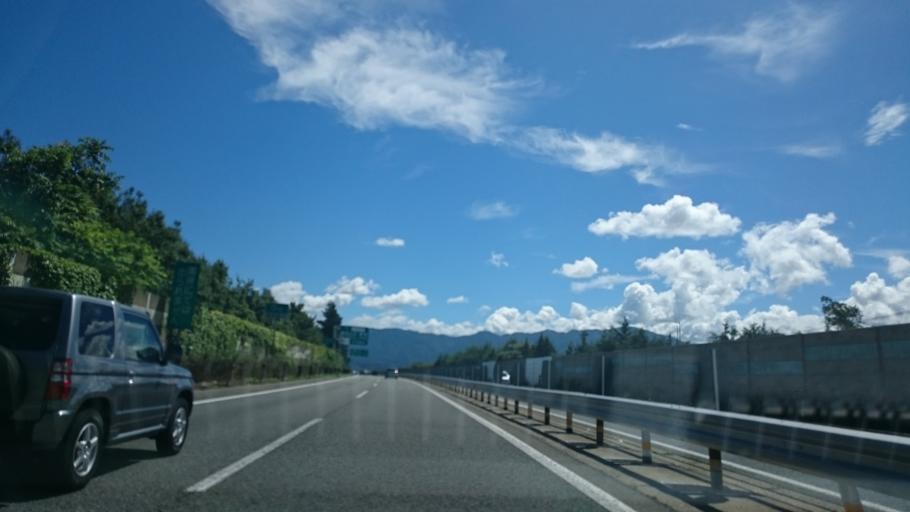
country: JP
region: Nagano
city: Iida
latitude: 35.4759
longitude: 137.7600
